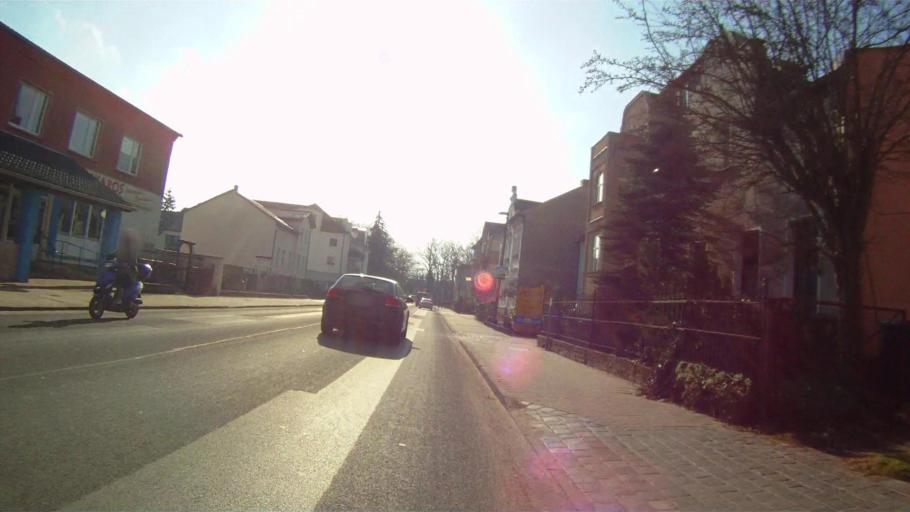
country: DE
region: Brandenburg
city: Erkner
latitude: 52.4186
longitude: 13.7541
